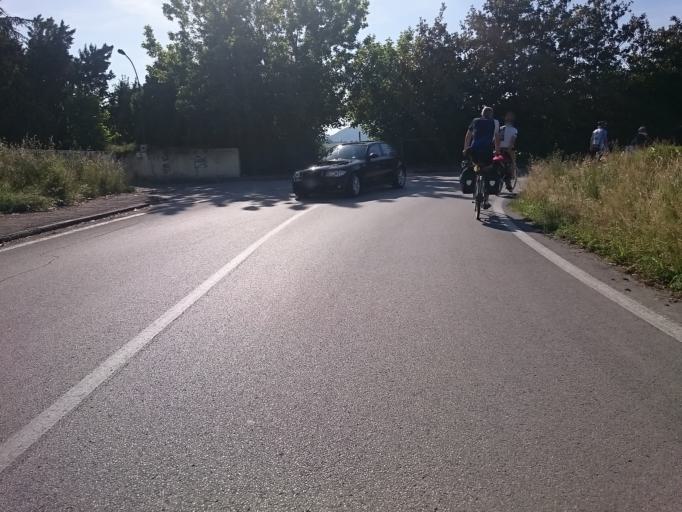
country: IT
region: Veneto
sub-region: Provincia di Padova
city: Torreglia
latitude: 45.3481
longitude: 11.7588
